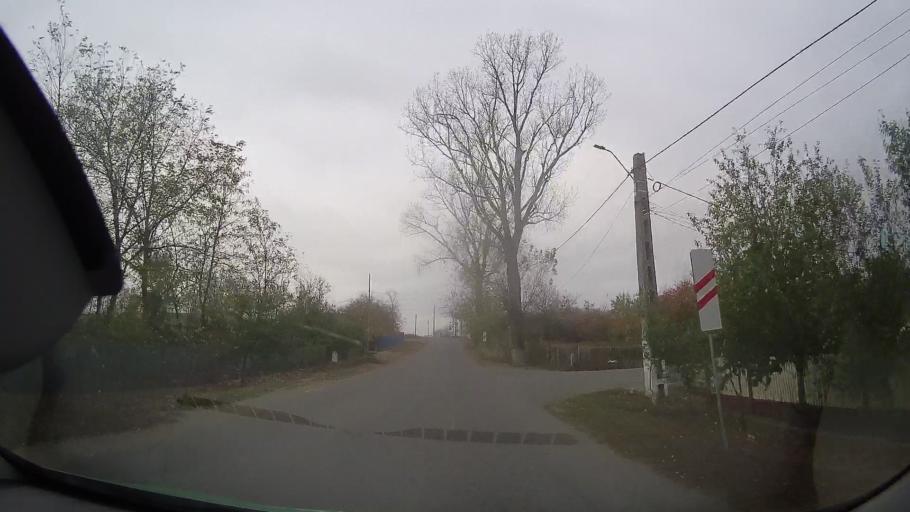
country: RO
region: Braila
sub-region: Comuna Ciresu
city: Ciresu
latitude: 44.9407
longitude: 27.3964
